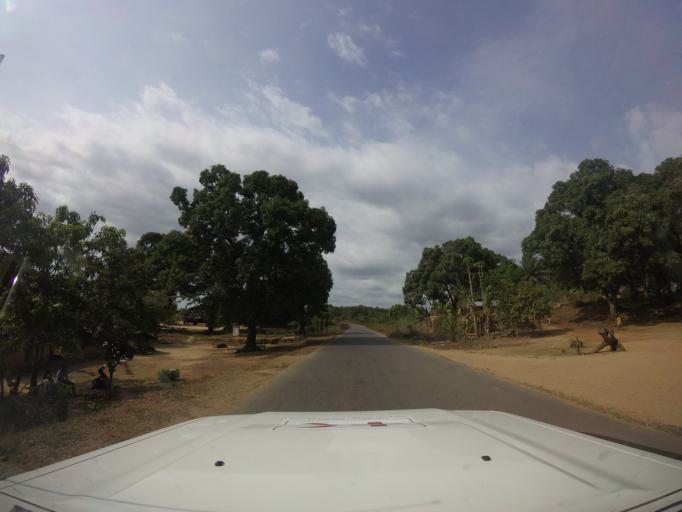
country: LR
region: Bomi
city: Tubmanburg
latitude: 6.6966
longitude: -10.8735
